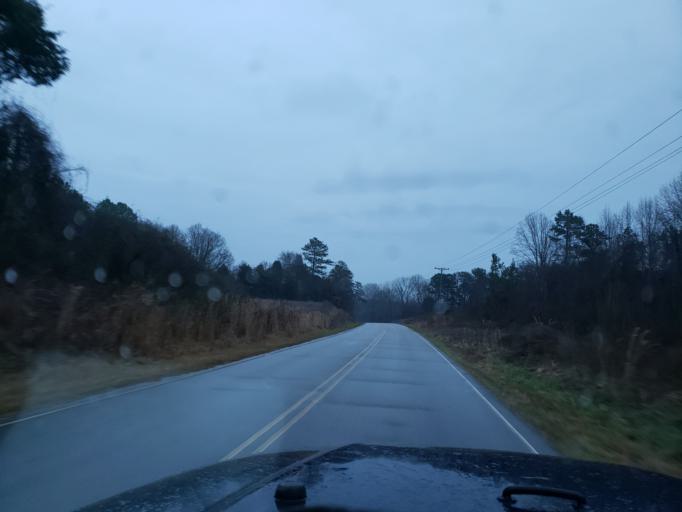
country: US
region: South Carolina
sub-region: Cherokee County
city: Blacksburg
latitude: 35.1570
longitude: -81.4600
